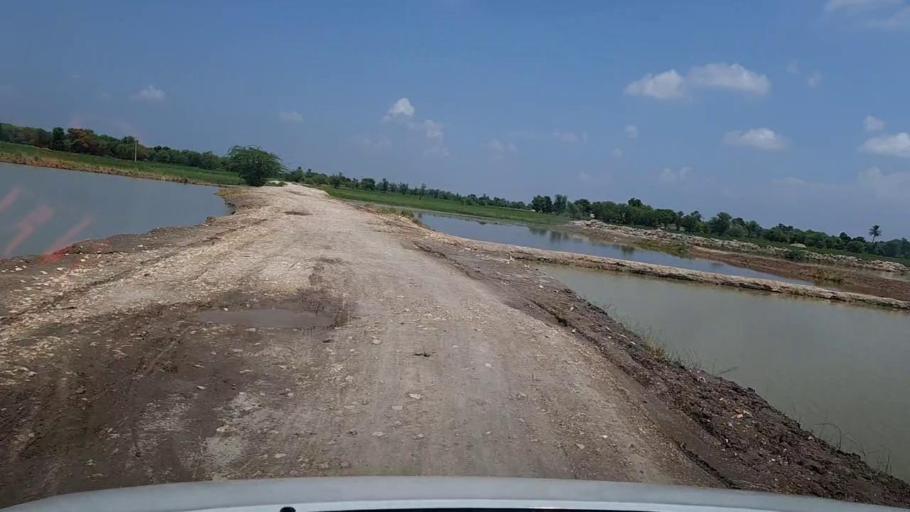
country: PK
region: Sindh
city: Kandiaro
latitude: 26.9856
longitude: 68.2352
